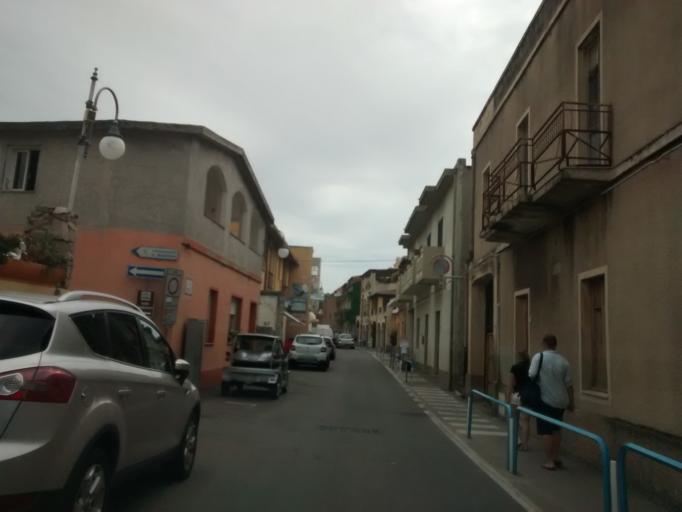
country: IT
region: Sardinia
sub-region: Provincia di Cagliari
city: Villasimius
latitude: 39.1436
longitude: 9.5180
